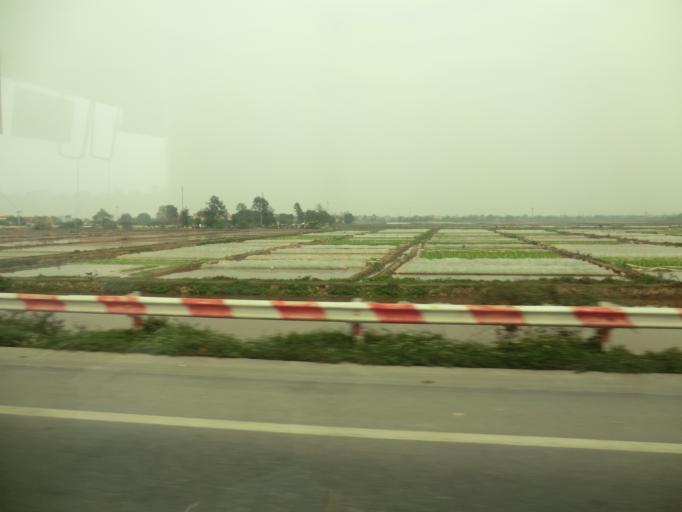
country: VN
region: Ha Noi
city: Phu Xuyen
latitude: 20.7213
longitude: 105.9182
